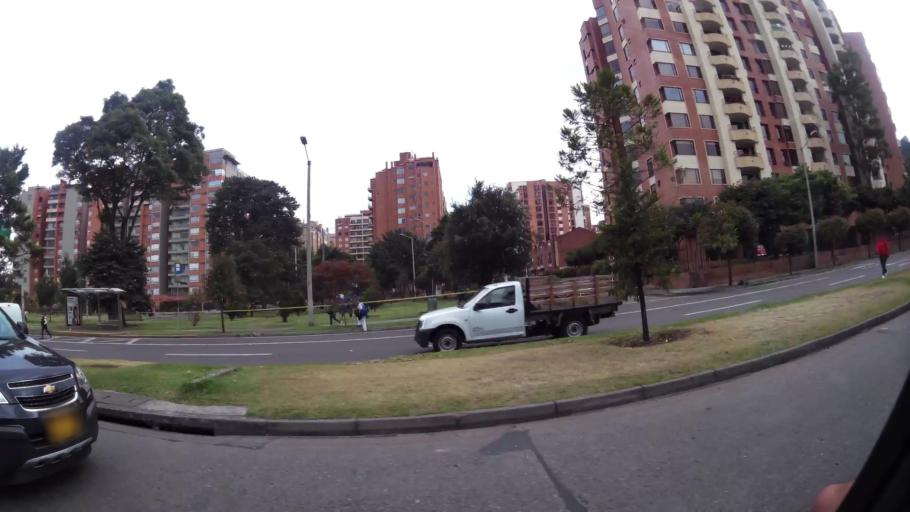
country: CO
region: Bogota D.C.
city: Barrio San Luis
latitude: 4.7122
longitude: -74.0315
